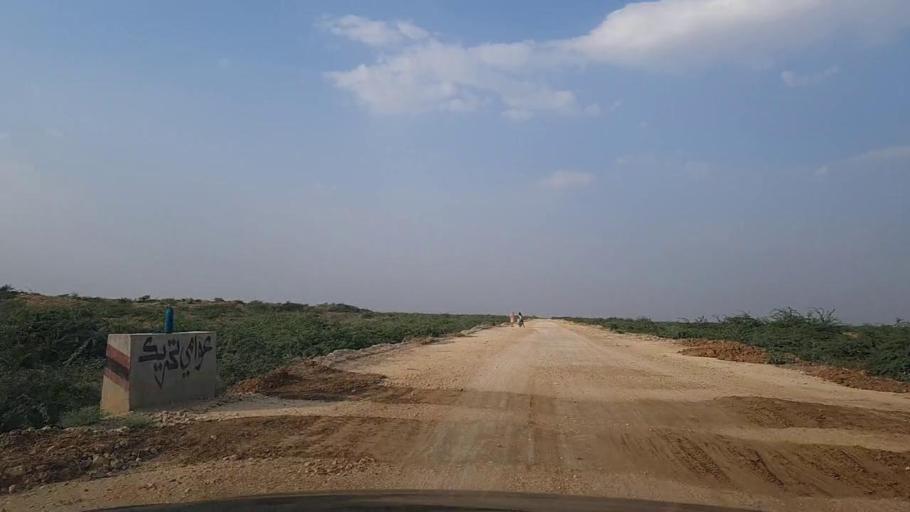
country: PK
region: Sindh
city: Gharo
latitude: 24.8320
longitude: 67.7454
